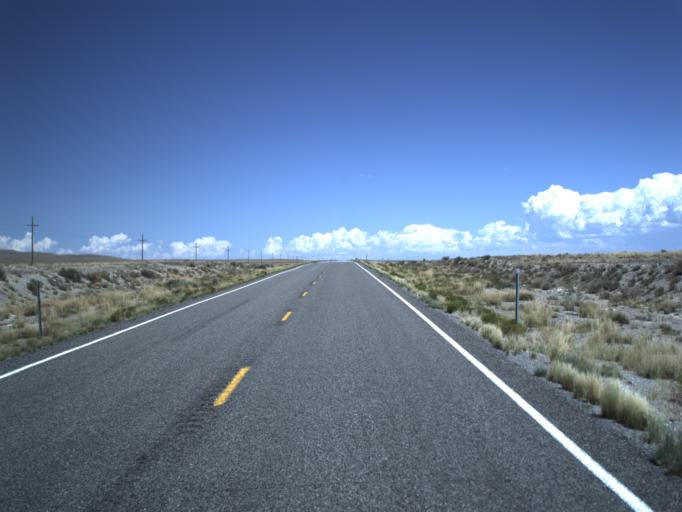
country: US
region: Utah
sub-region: Millard County
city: Delta
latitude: 39.1301
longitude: -113.1037
